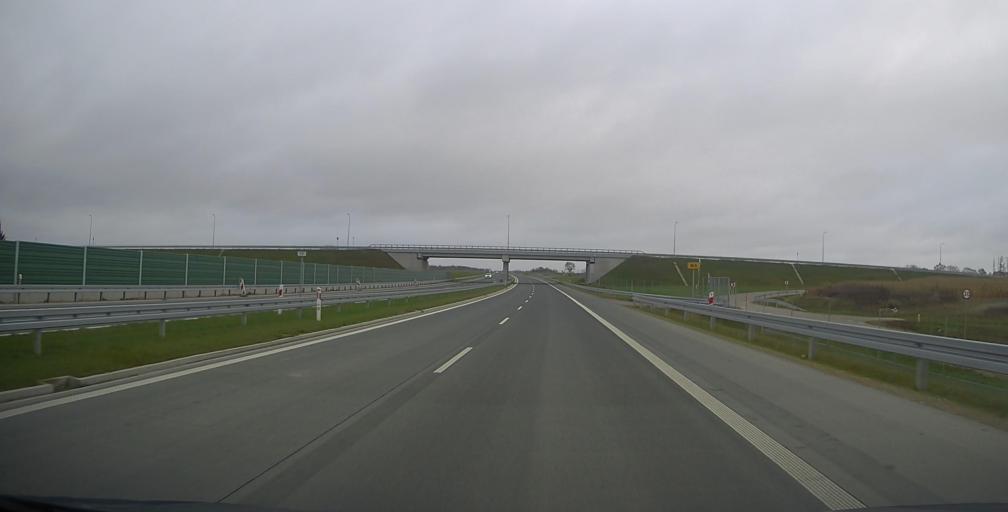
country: PL
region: Podlasie
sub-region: Powiat grajewski
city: Rajgrod
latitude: 53.8793
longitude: 22.6631
